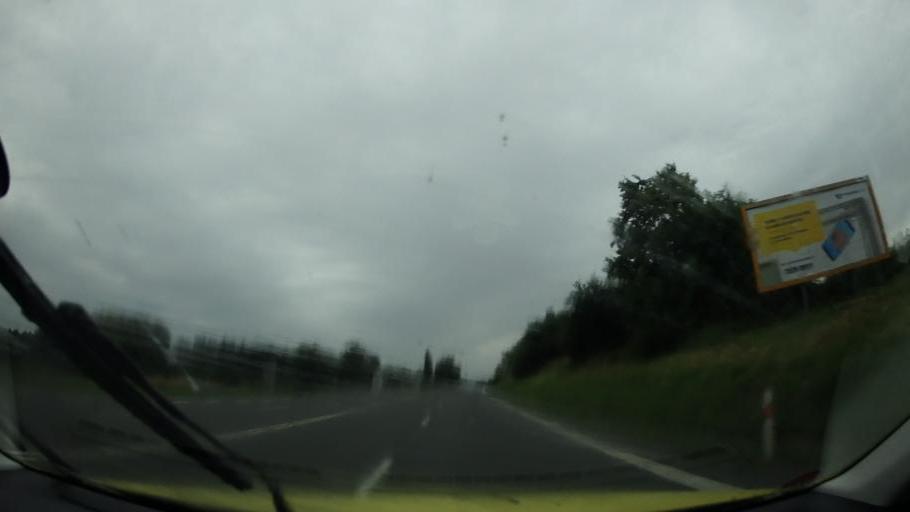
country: CZ
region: Olomoucky
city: Belotin
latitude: 49.5744
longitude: 17.7764
